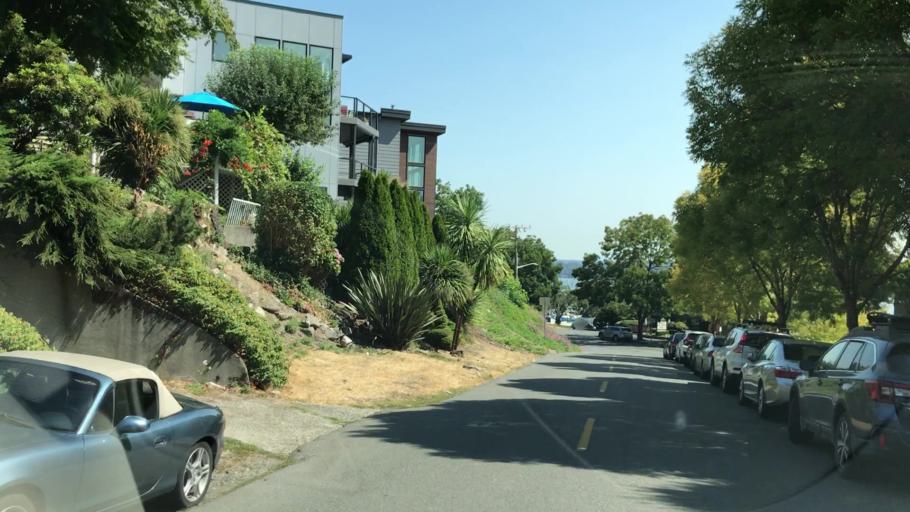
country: US
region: Washington
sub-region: King County
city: Seattle
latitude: 47.6024
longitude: -122.2858
